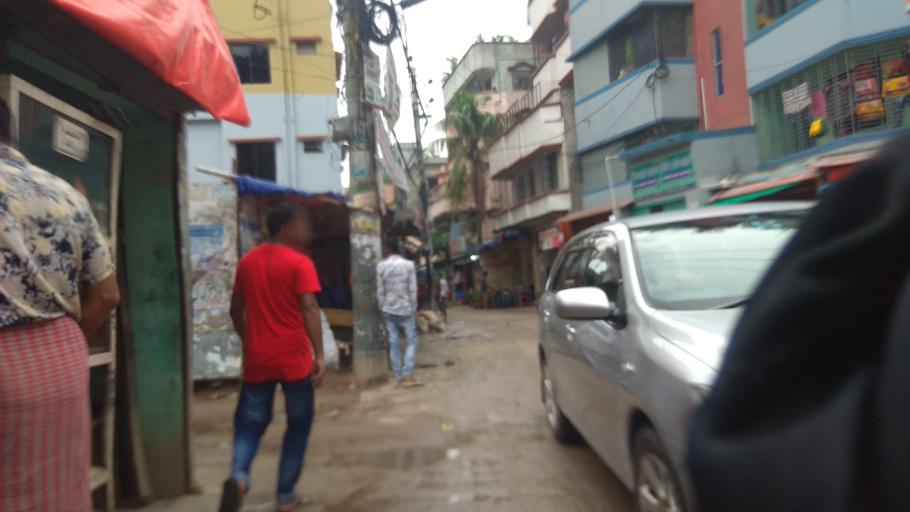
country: BD
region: Dhaka
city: Azimpur
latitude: 23.7965
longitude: 90.3600
